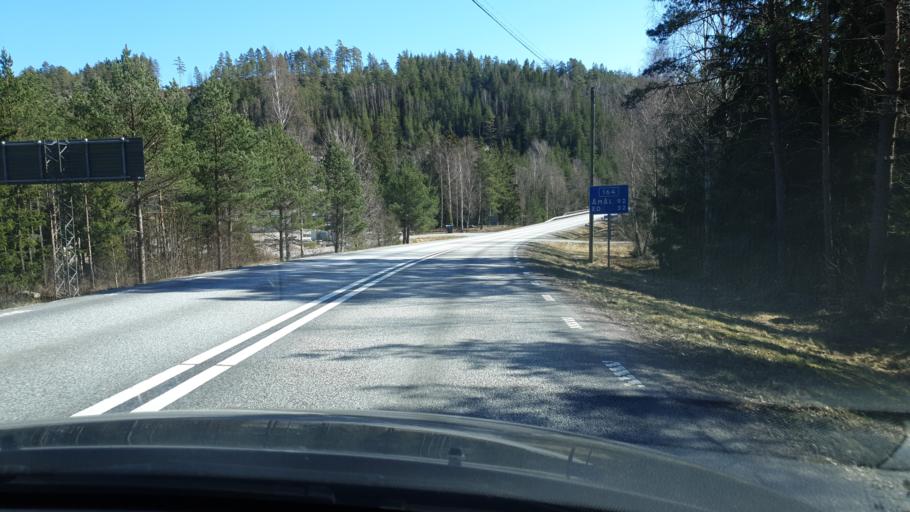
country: SE
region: Vaestra Goetaland
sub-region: Tanums Kommun
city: Tanumshede
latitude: 58.7973
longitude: 11.5665
